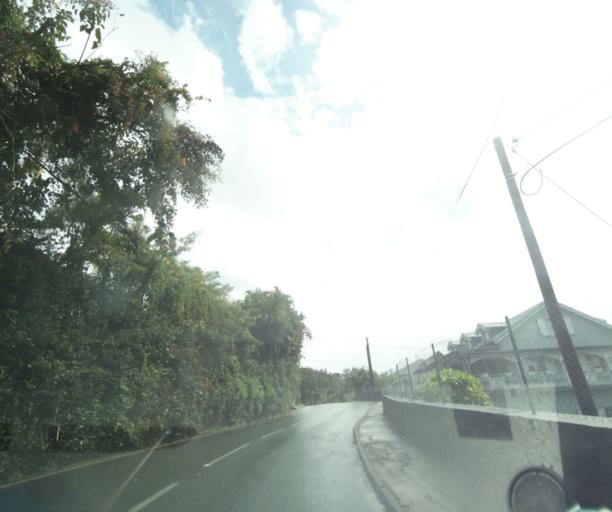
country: RE
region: Reunion
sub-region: Reunion
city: Saint-Paul
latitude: -20.9942
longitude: 55.3309
